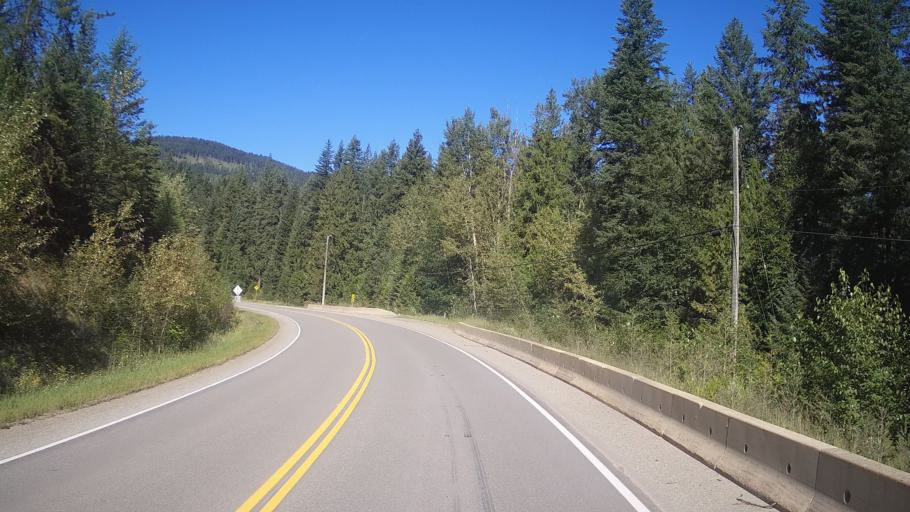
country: CA
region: British Columbia
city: Kamloops
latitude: 51.4536
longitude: -120.2178
